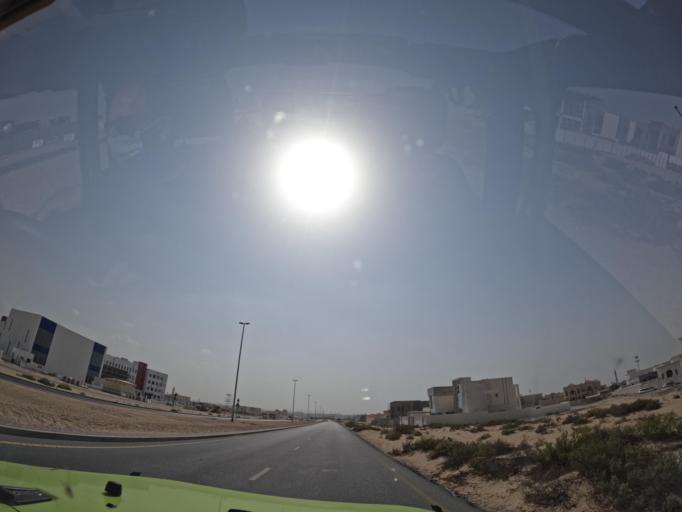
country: AE
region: Ash Shariqah
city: Sharjah
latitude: 25.1914
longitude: 55.4284
